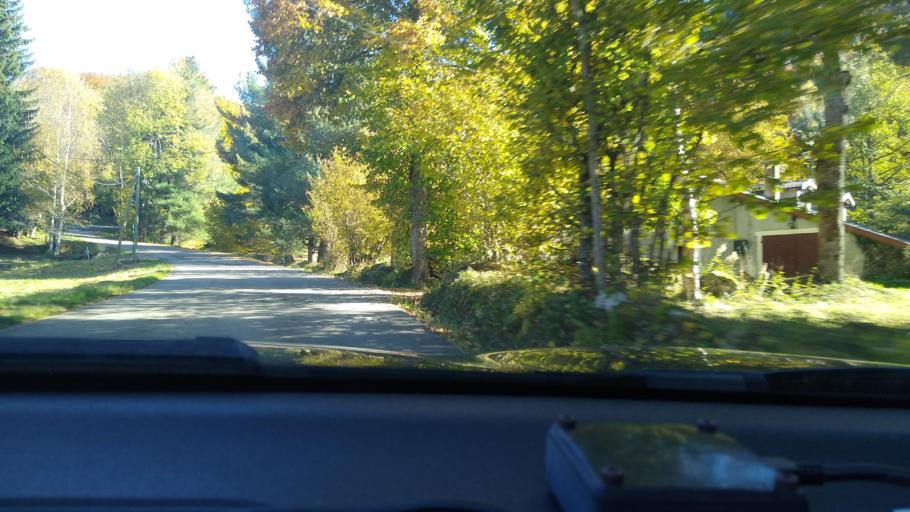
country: FR
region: Midi-Pyrenees
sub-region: Departement de l'Ariege
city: Ax-les-Thermes
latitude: 42.7207
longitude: 1.9052
